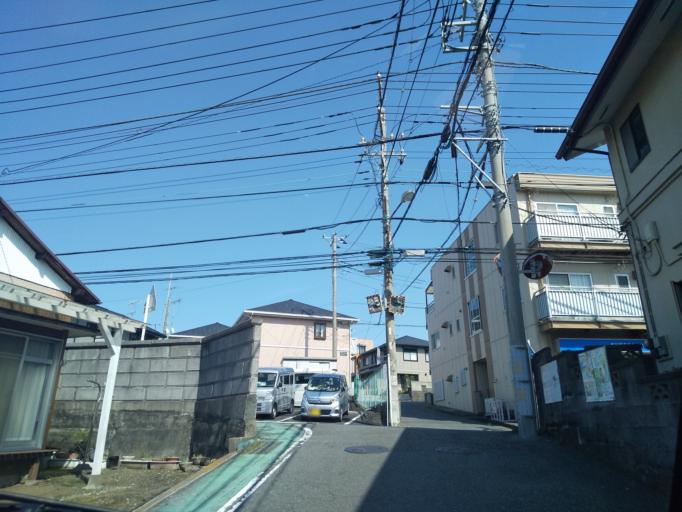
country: JP
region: Kanagawa
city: Zama
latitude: 35.4648
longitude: 139.4170
